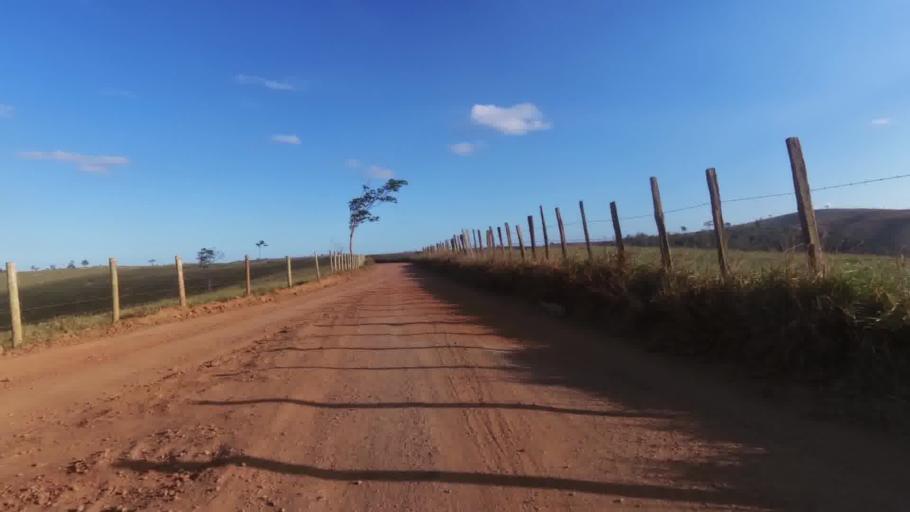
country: BR
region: Espirito Santo
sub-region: Marataizes
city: Marataizes
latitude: -21.1464
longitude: -41.0675
